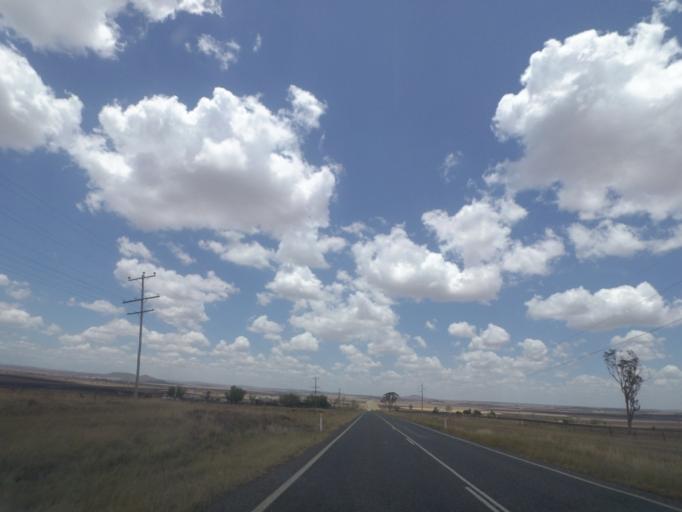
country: AU
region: Queensland
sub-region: Toowoomba
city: Top Camp
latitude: -27.8864
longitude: 151.9716
